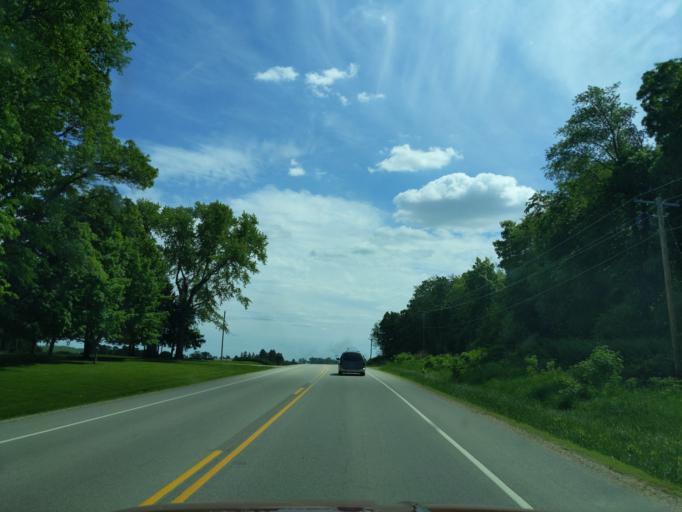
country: US
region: Wisconsin
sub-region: Columbia County
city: Poynette
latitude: 43.3486
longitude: -89.3283
